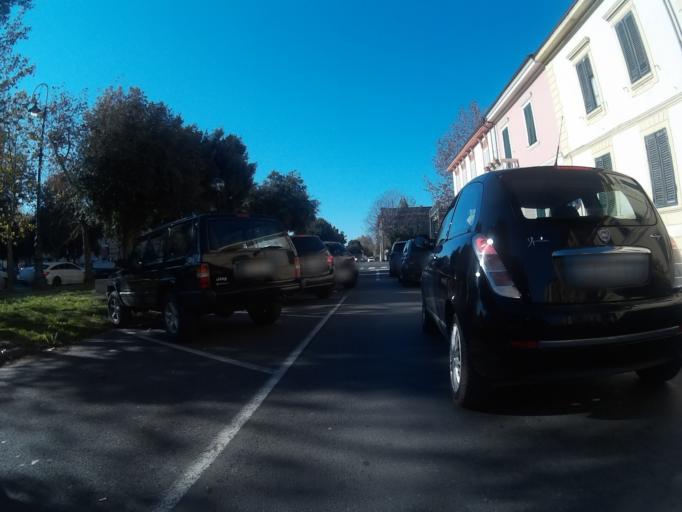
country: IT
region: Tuscany
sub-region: Provincia di Livorno
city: Livorno
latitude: 43.5539
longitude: 10.3282
